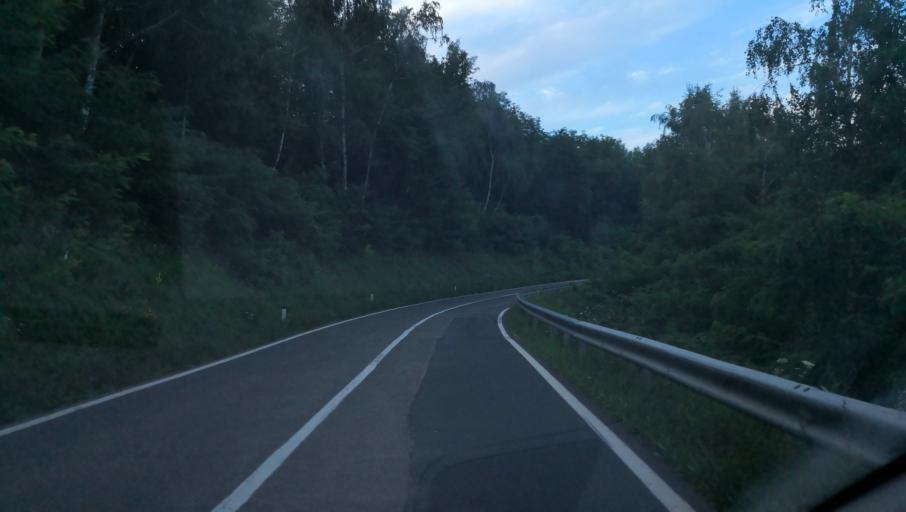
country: SI
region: Metlika
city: Metlika
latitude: 45.6961
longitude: 15.2600
